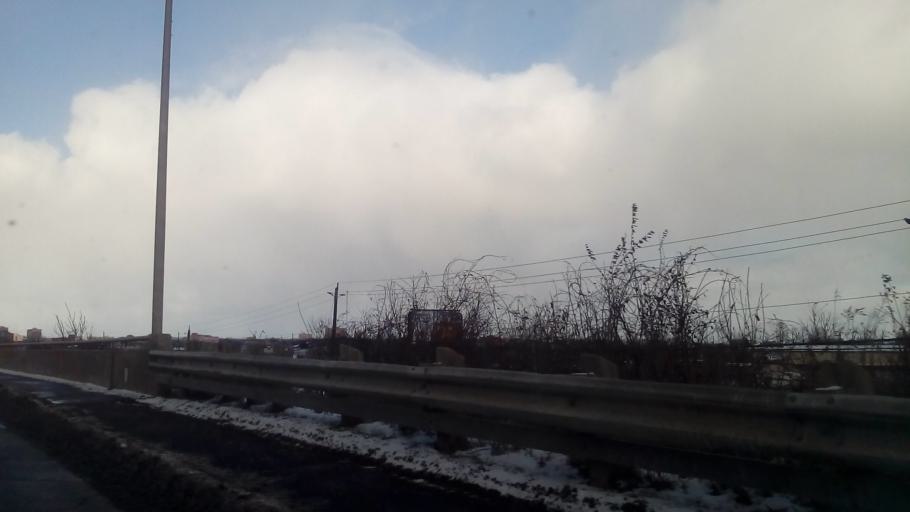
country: CA
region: Ontario
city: Ottawa
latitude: 45.4086
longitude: -75.6284
